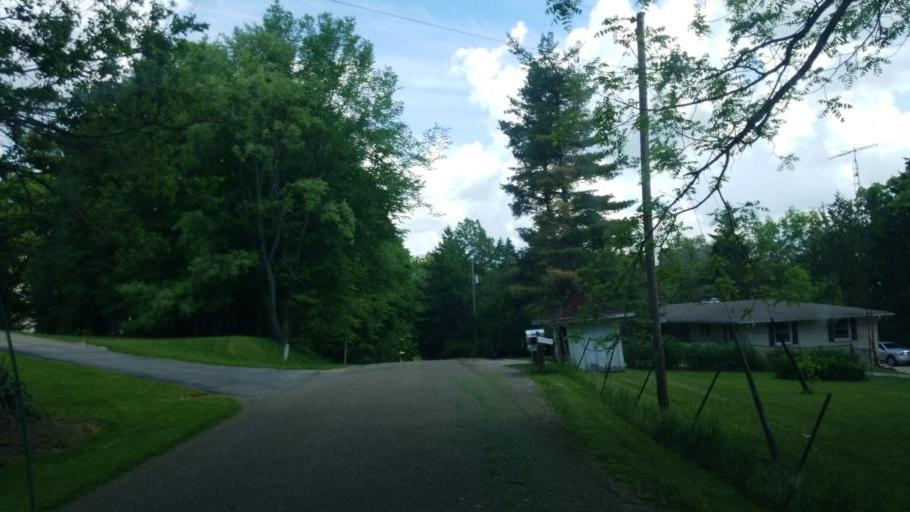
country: US
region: Ohio
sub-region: Sandusky County
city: Bellville
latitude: 40.6436
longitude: -82.5225
